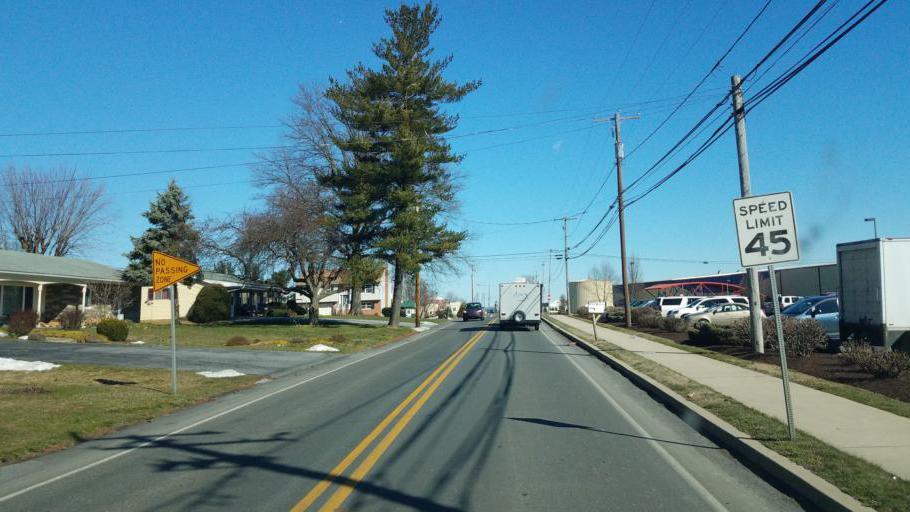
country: US
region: Pennsylvania
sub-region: Lancaster County
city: New Holland
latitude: 40.0952
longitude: -76.1129
